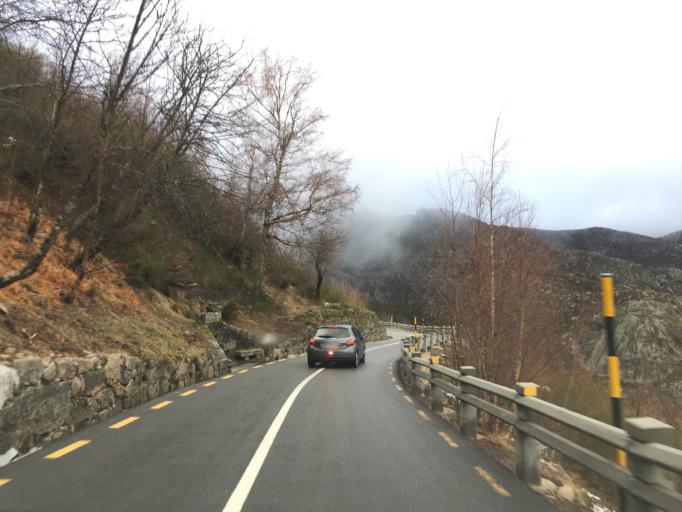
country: PT
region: Castelo Branco
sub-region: Covilha
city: Covilha
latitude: 40.3244
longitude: -7.5774
